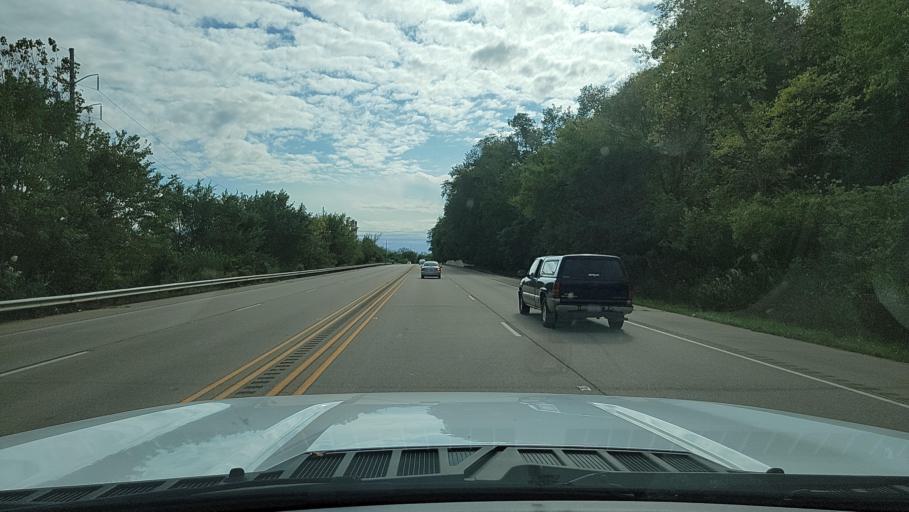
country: US
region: Illinois
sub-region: Peoria County
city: Bartonville
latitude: 40.6157
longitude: -89.6581
